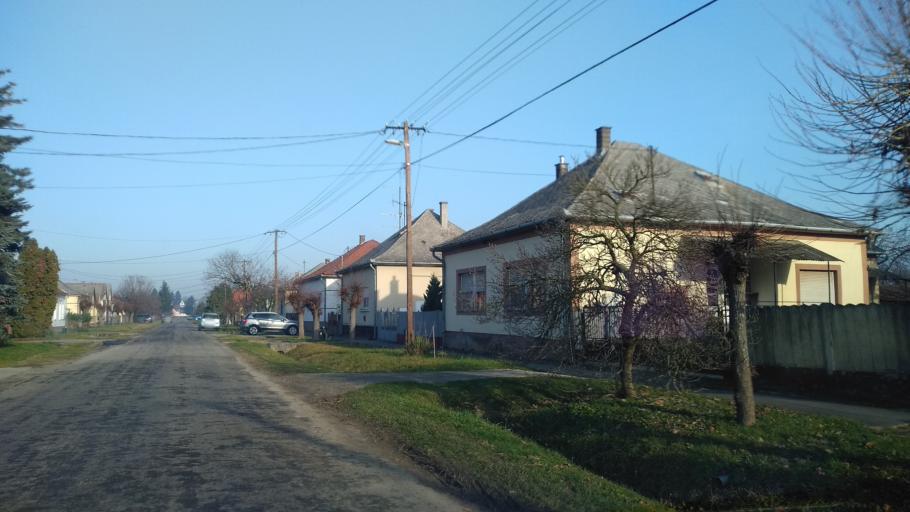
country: HU
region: Somogy
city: Barcs
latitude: 45.9613
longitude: 17.4749
